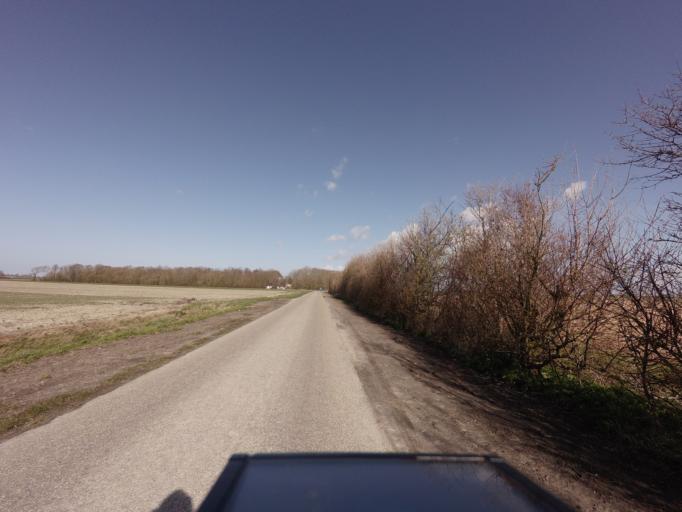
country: NL
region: Zeeland
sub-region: Schouwen-Duiveland
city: Scharendijke
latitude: 51.7078
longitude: 3.8192
